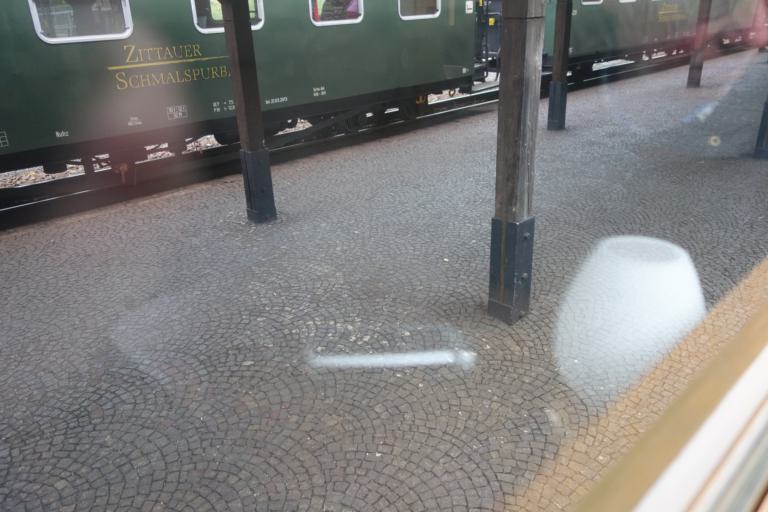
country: DE
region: Saxony
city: Zittau
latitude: 50.8902
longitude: 14.7918
